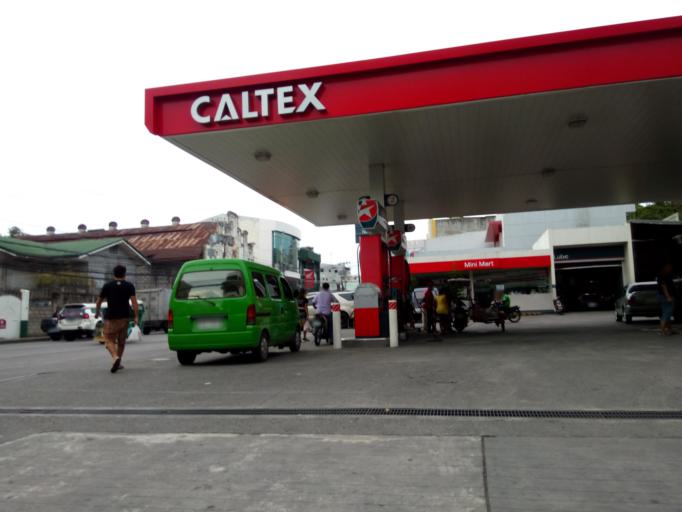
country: PH
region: Central Visayas
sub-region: Province of Negros Oriental
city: Dumaguete
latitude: 9.3069
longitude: 123.3059
